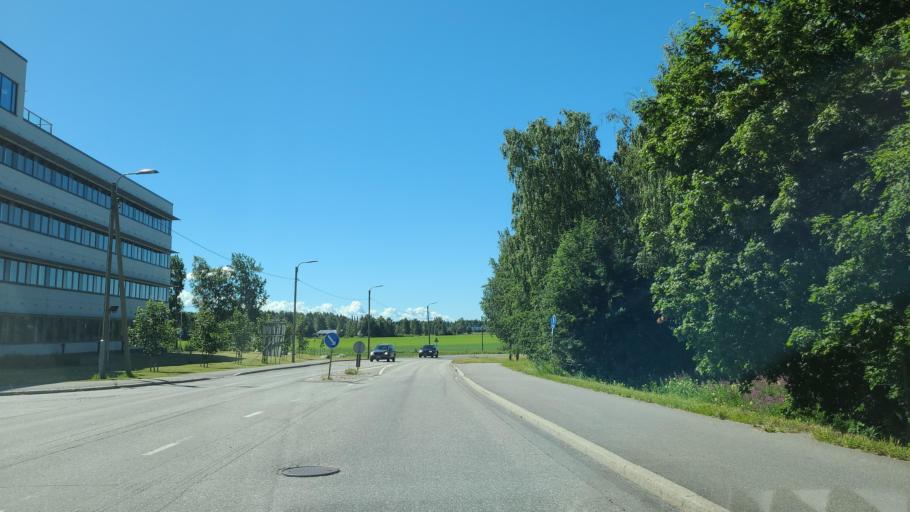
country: FI
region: Ostrobothnia
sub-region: Vaasa
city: Ristinummi
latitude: 63.0572
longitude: 21.7311
